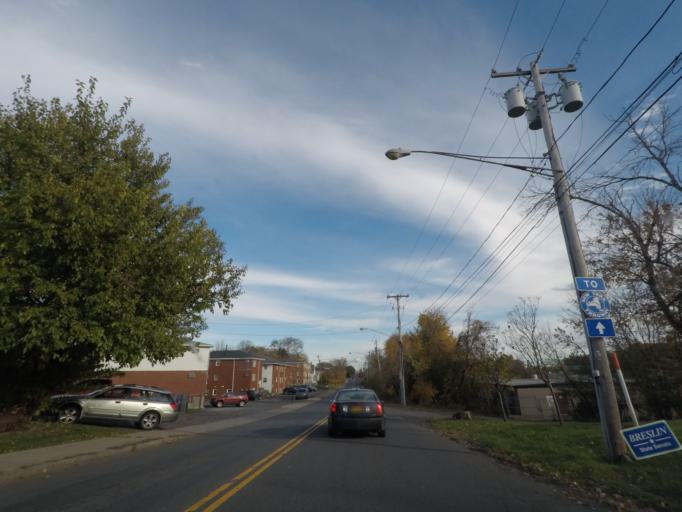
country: US
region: New York
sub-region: Albany County
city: Albany
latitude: 42.6377
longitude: -73.7897
